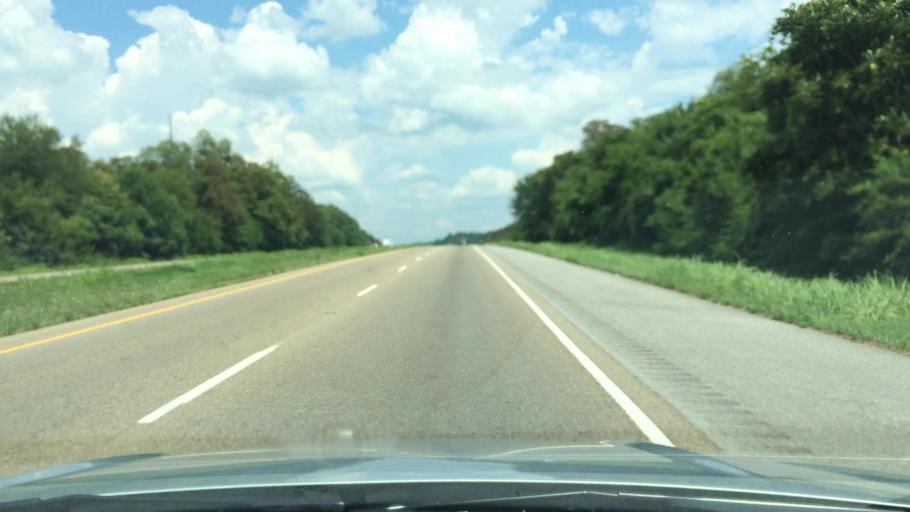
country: US
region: Tennessee
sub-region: Hamblen County
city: Morristown
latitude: 36.1801
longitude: -83.3335
